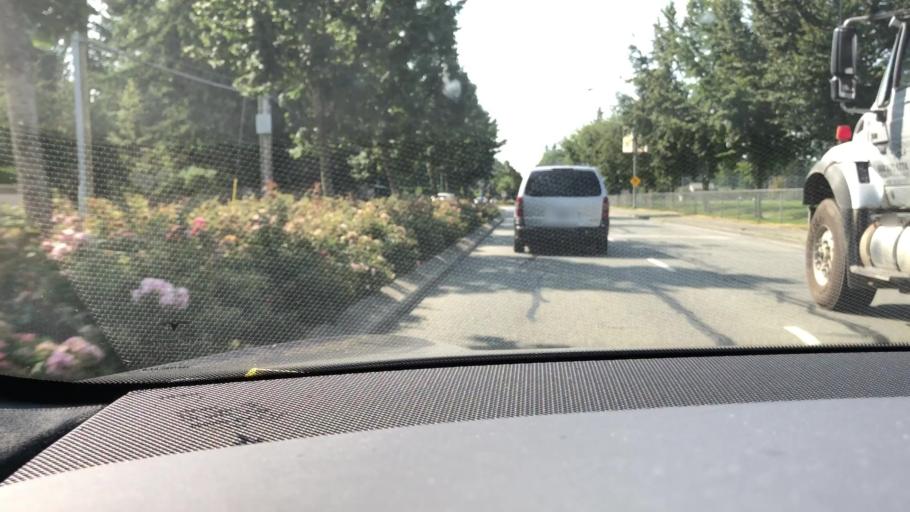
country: US
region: Washington
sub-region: Whatcom County
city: Point Roberts
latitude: 49.0220
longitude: -123.0688
